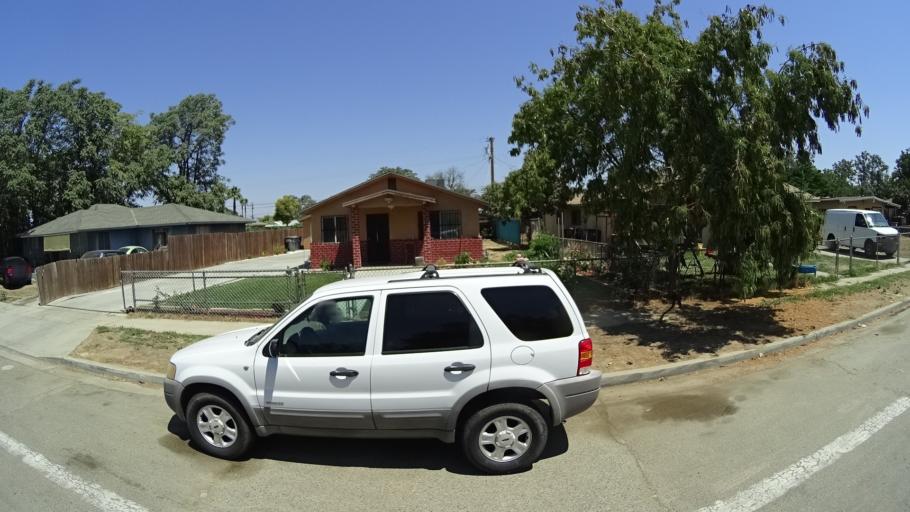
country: US
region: California
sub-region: Fresno County
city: West Park
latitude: 36.7086
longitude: -119.8081
